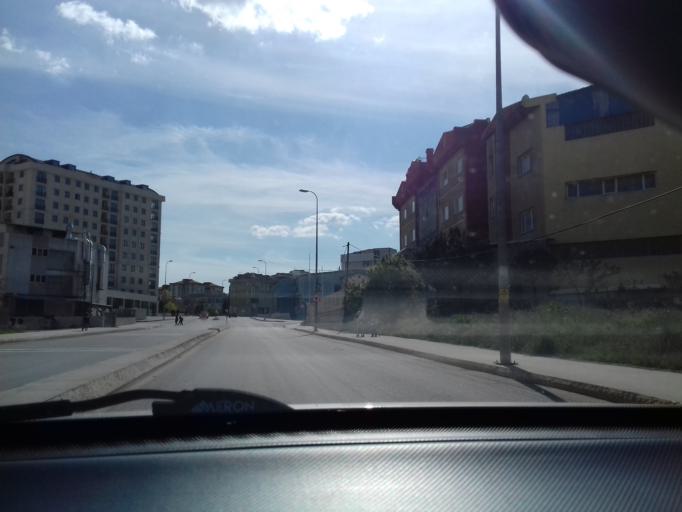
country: TR
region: Istanbul
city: Pendik
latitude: 40.8925
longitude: 29.2706
